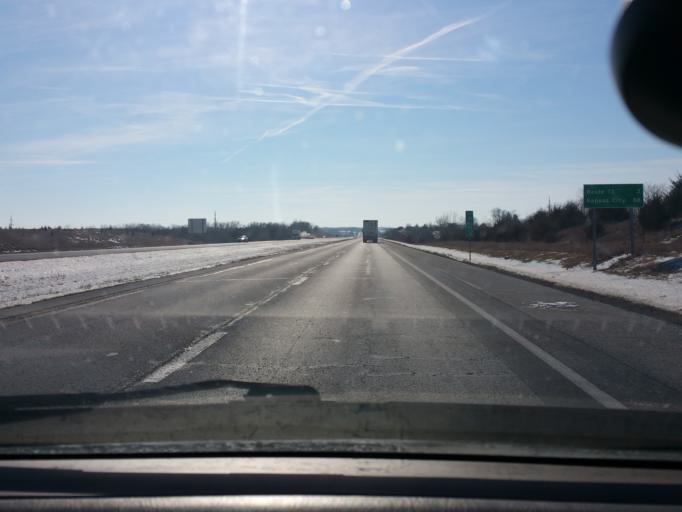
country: US
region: Missouri
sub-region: Harrison County
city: Bethany
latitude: 40.2538
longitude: -94.0131
